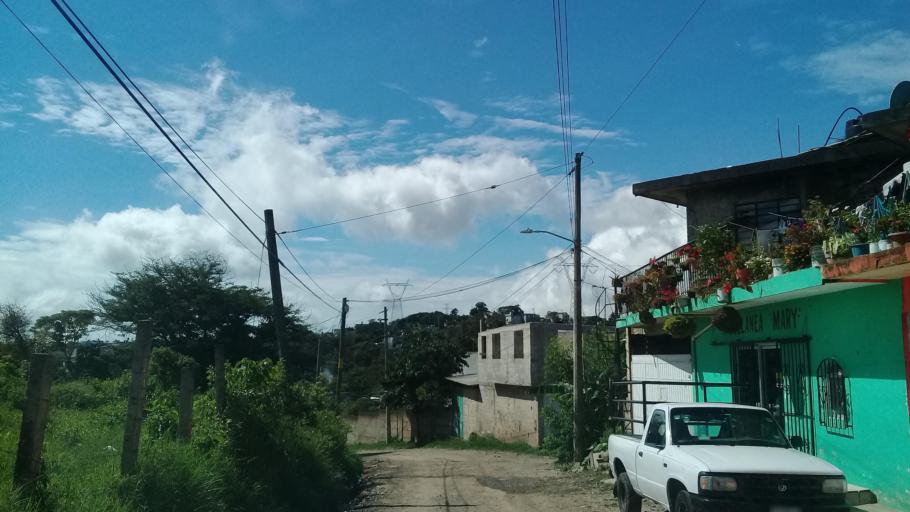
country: MX
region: Veracruz
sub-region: Jilotepec
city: El Pueblito (Garbanzal)
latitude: 19.5732
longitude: -96.8986
